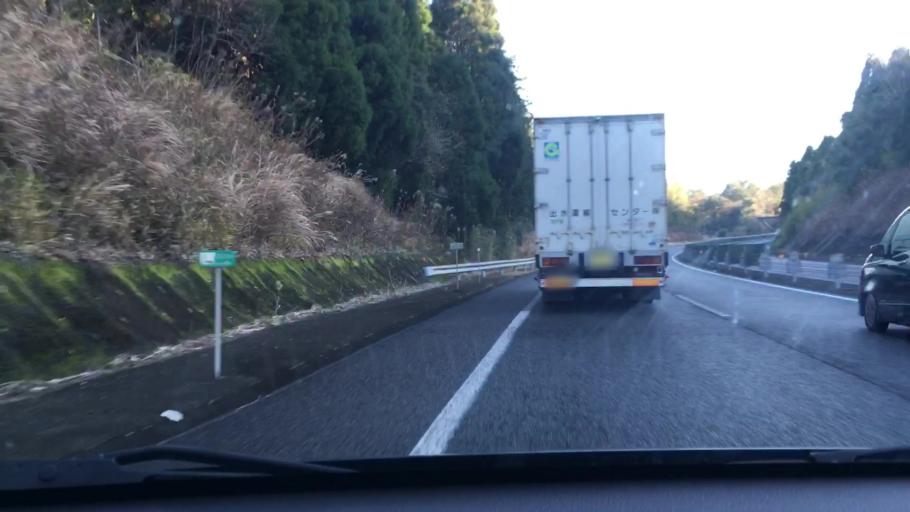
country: JP
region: Kagoshima
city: Kajiki
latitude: 31.8318
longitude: 130.6927
